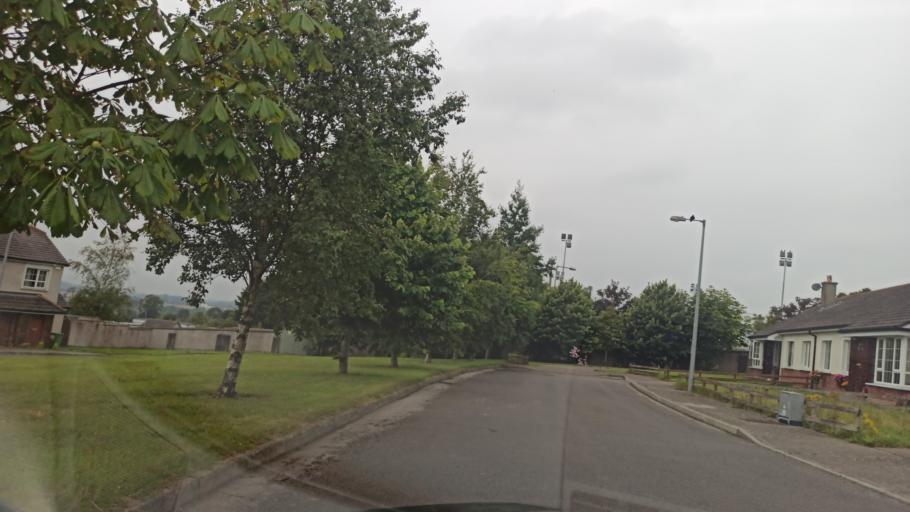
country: IE
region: Munster
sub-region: South Tipperary
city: Cluain Meala
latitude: 52.3689
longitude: -7.7171
